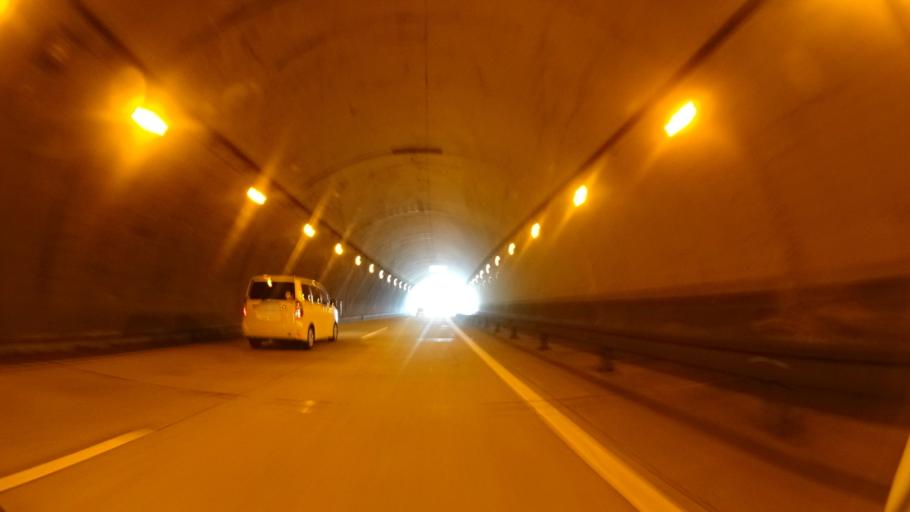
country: JP
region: Hyogo
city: Akashi
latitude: 34.5276
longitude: 134.9440
